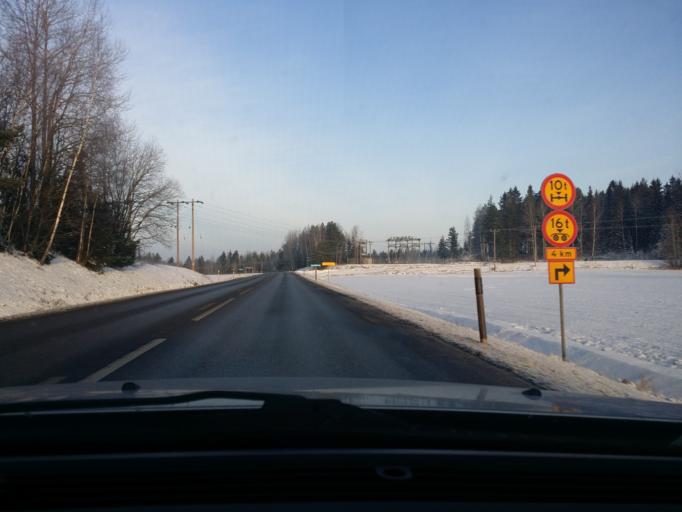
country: SE
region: OErebro
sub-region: Lindesbergs Kommun
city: Frovi
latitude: 59.5011
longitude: 15.3752
